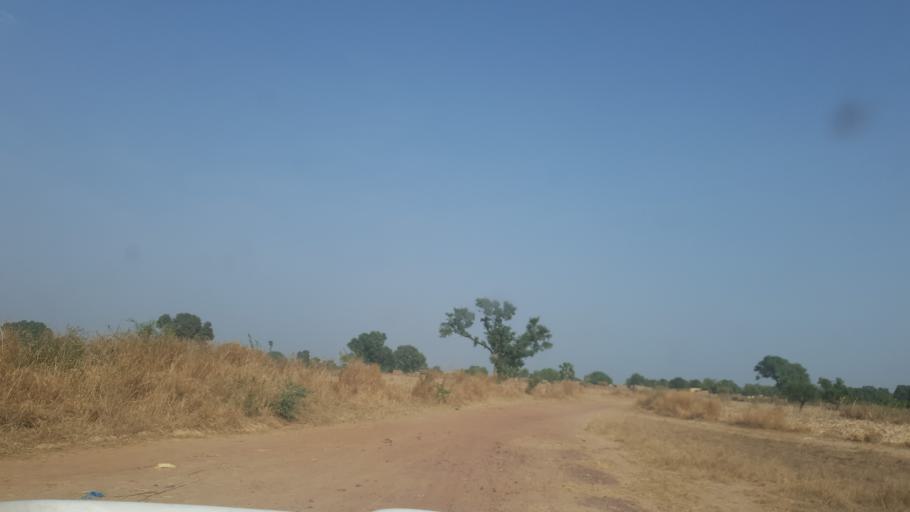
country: ML
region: Segou
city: Baroueli
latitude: 13.3534
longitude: -6.9374
